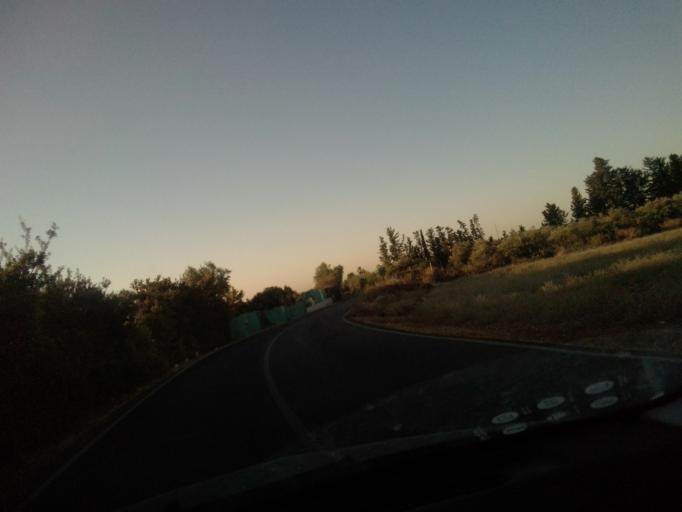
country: CY
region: Limassol
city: Ypsonas
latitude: 34.6709
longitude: 32.9598
